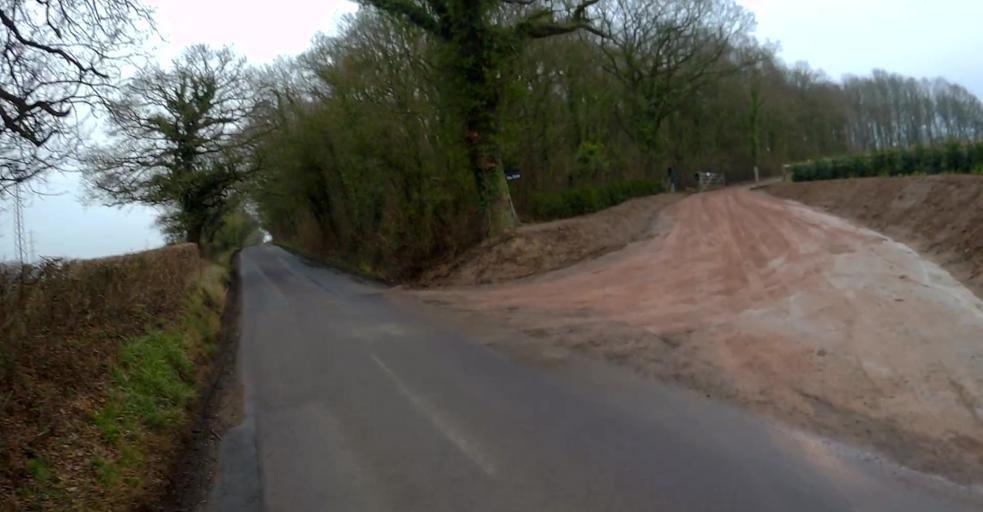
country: GB
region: England
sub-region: Hampshire
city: Old Basing
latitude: 51.2812
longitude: -1.0317
